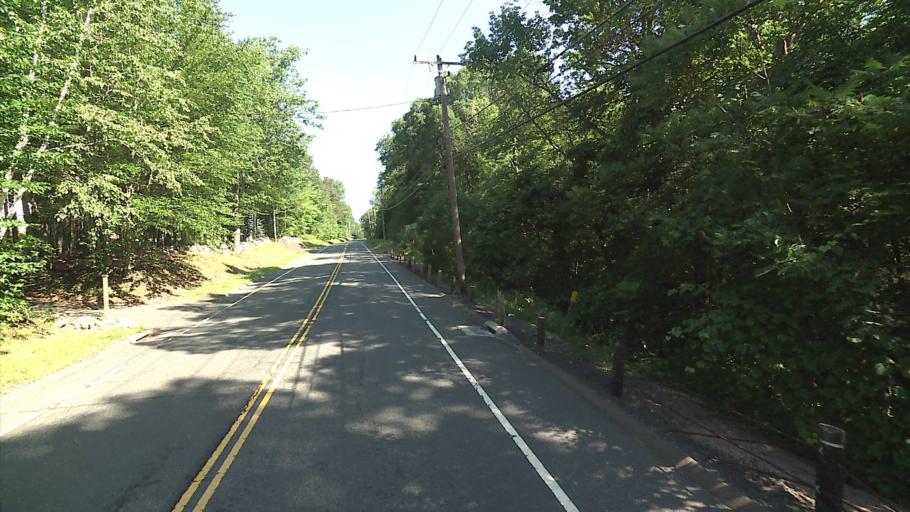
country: US
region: Connecticut
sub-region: Hartford County
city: North Granby
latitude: 41.9809
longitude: -72.8898
